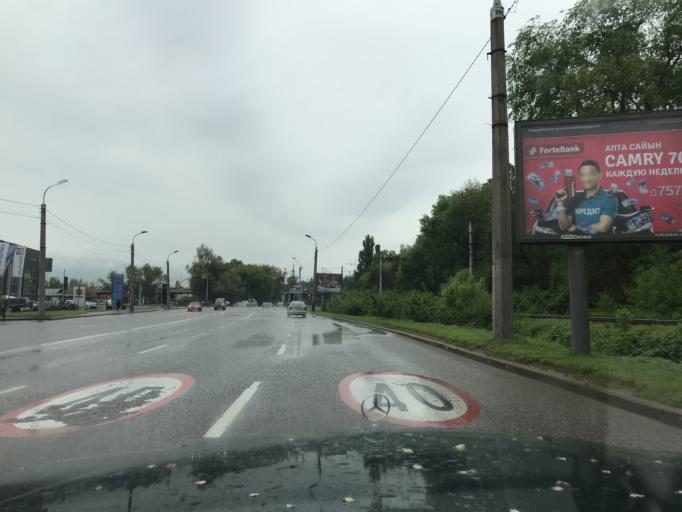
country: KZ
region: Almaty Qalasy
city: Almaty
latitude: 43.2969
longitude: 76.9487
